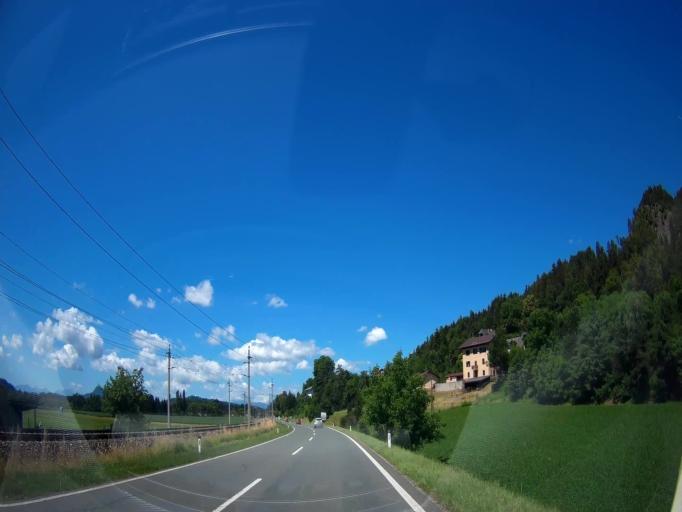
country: AT
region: Carinthia
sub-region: Politischer Bezirk Sankt Veit an der Glan
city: St. Georgen am Laengsee
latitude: 46.7627
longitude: 14.4323
